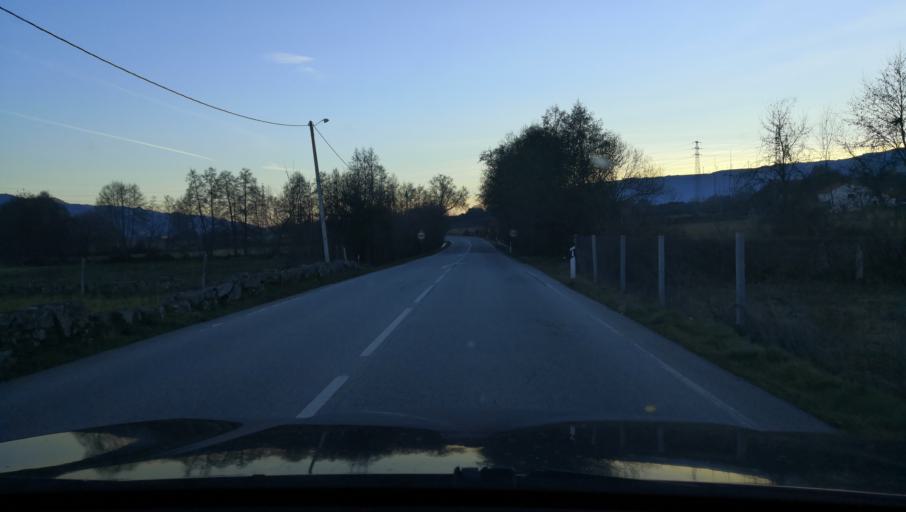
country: PT
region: Vila Real
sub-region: Vila Pouca de Aguiar
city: Vila Pouca de Aguiar
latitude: 41.4684
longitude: -7.6642
